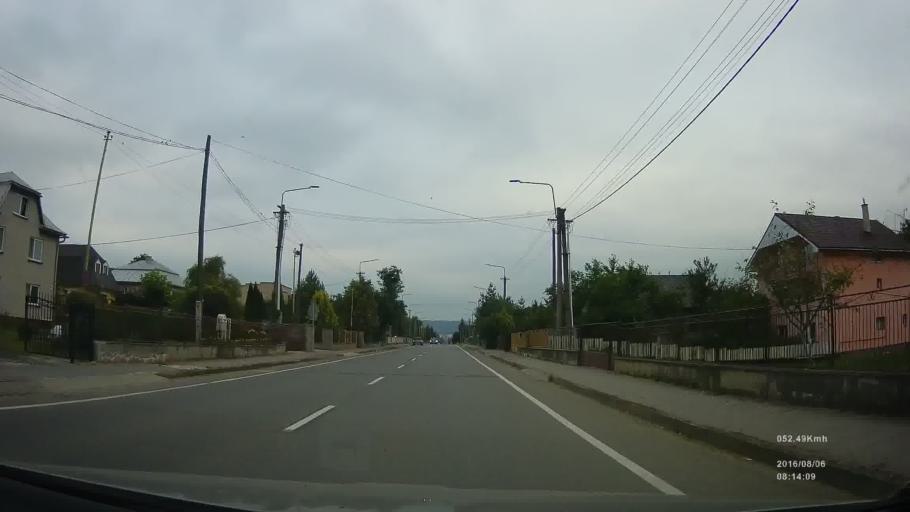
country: SK
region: Presovsky
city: Stropkov
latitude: 49.2187
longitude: 21.6607
